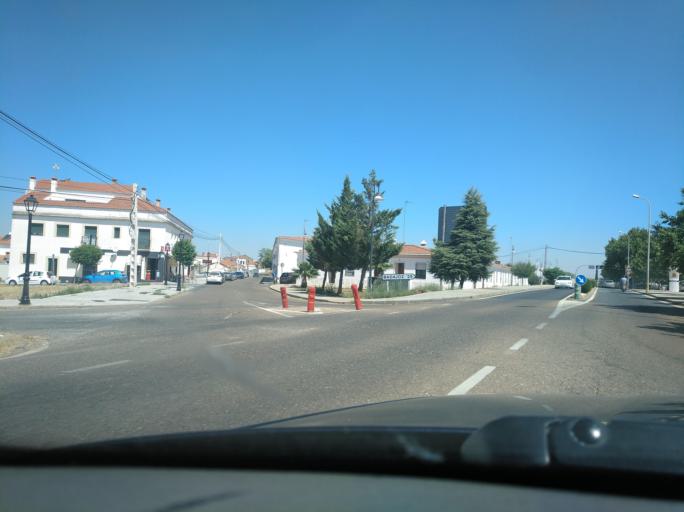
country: ES
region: Extremadura
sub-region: Provincia de Badajoz
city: Olivenza
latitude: 38.6782
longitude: -7.0964
